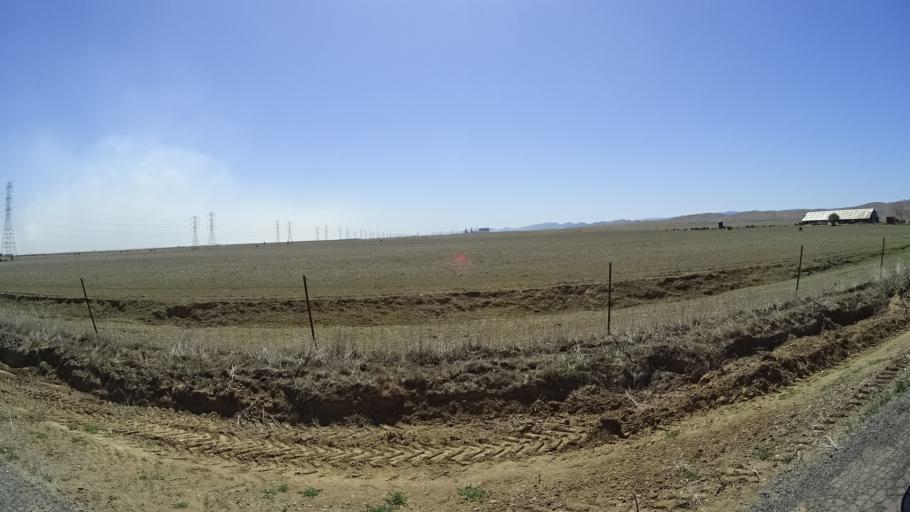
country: US
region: California
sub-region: Glenn County
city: Willows
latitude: 39.3999
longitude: -122.2654
